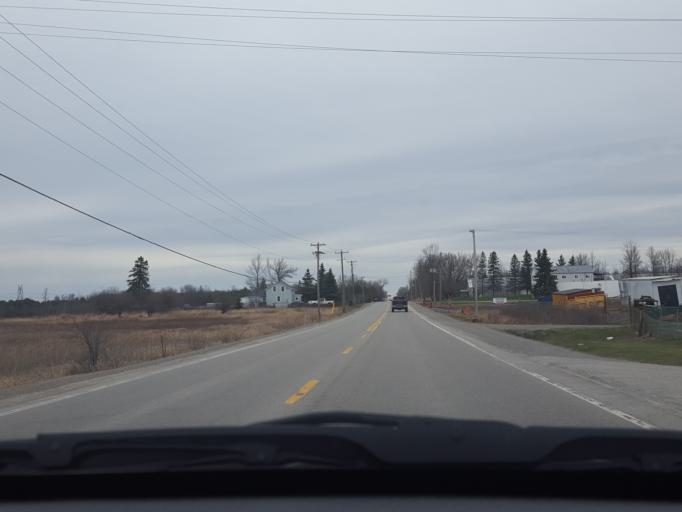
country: CA
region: Ontario
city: Uxbridge
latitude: 44.3281
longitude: -79.1847
